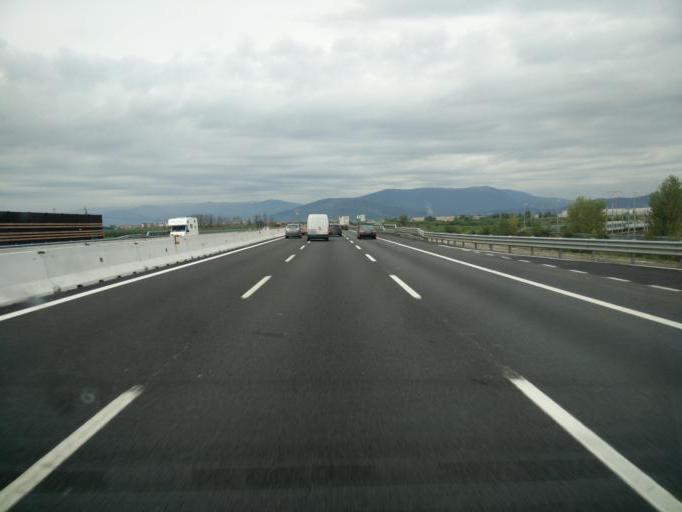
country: IT
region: Tuscany
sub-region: Province of Florence
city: San Donnino
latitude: 43.7992
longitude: 11.1554
